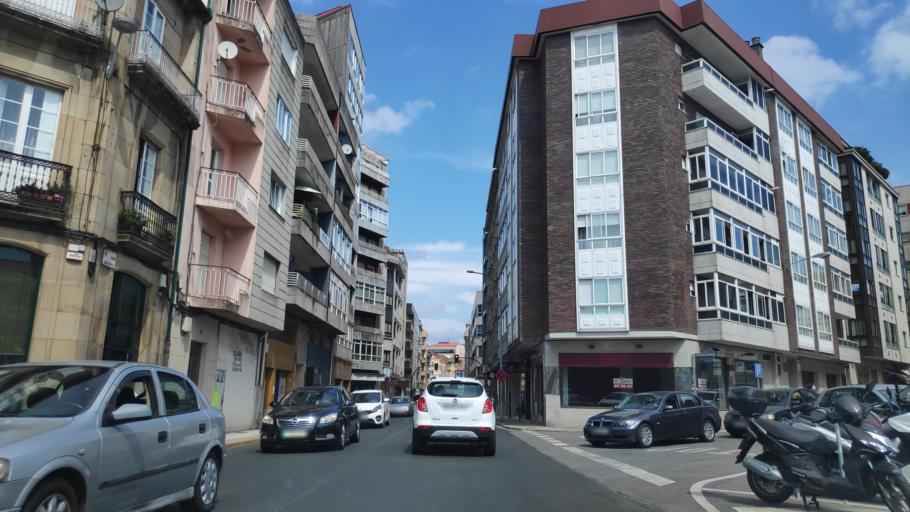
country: ES
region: Galicia
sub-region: Provincia de Pontevedra
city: Vilagarcia de Arousa
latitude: 42.5970
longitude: -8.7639
